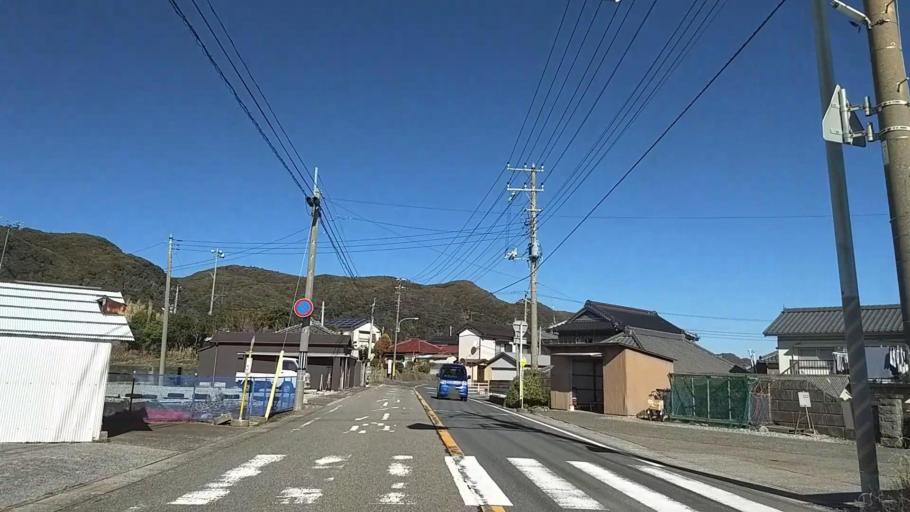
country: JP
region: Chiba
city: Tateyama
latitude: 34.9218
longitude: 139.9389
